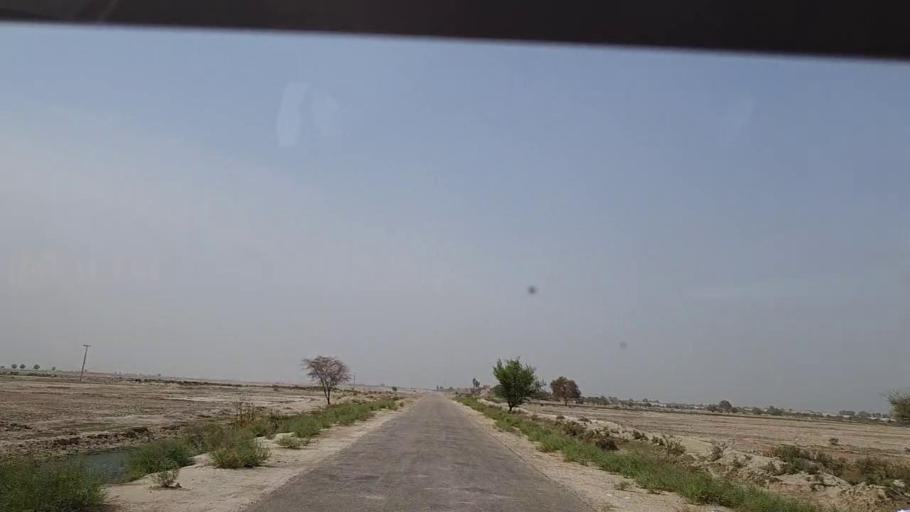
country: PK
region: Sindh
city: Khairpur Nathan Shah
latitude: 27.0593
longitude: 67.6480
